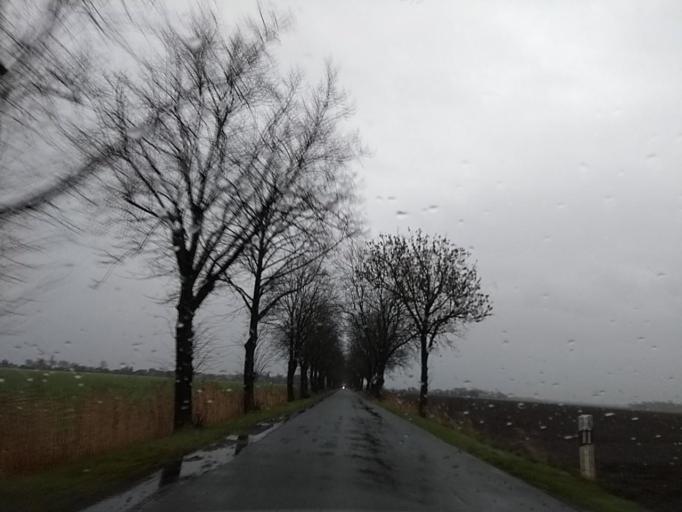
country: DE
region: Lower Saxony
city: Bunde
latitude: 53.2618
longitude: 7.2448
